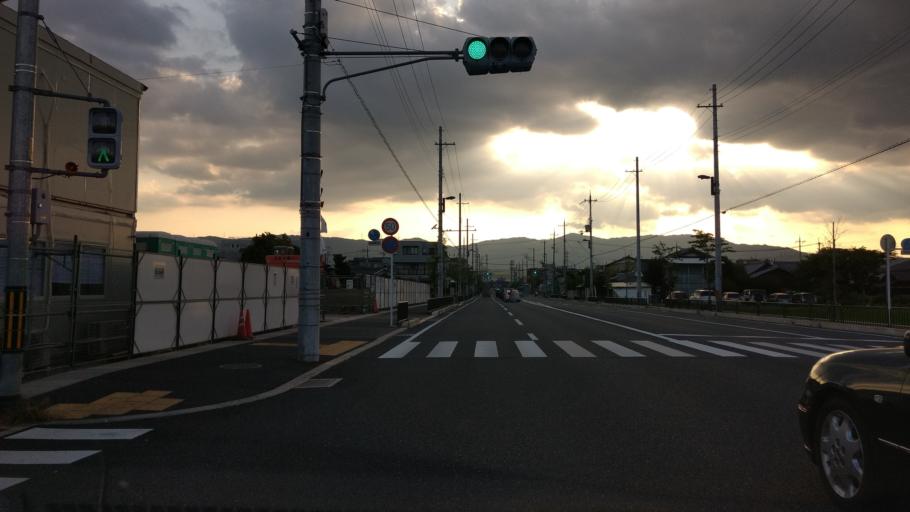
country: JP
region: Kyoto
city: Muko
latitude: 34.9547
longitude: 135.7224
